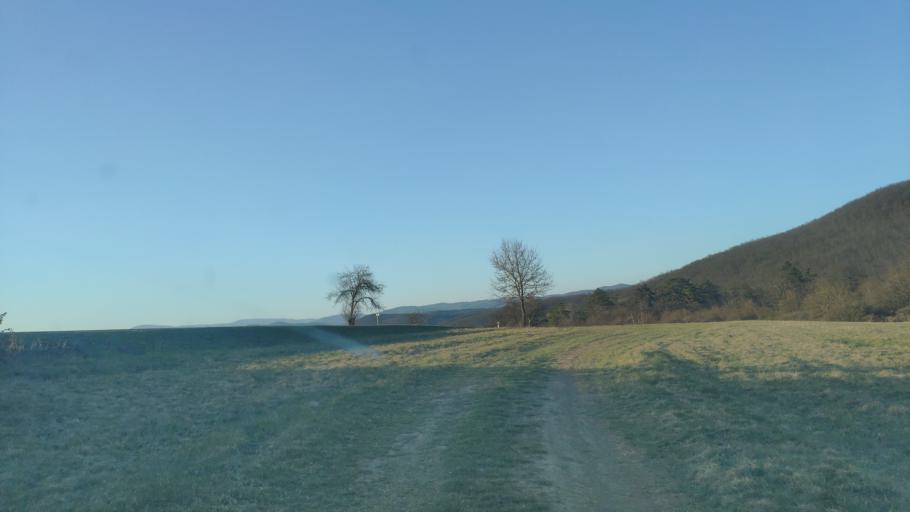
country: SK
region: Banskobystricky
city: Revuca
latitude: 48.5228
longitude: 20.3058
